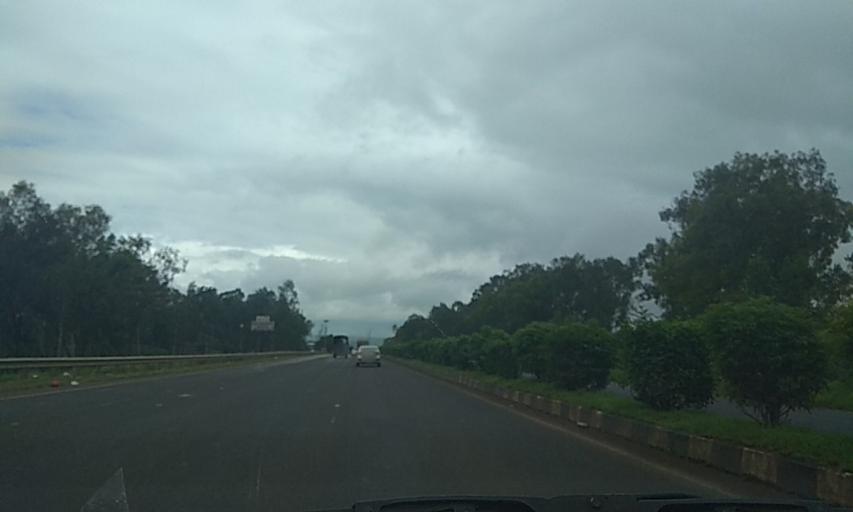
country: IN
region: Karnataka
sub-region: Belgaum
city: Belgaum
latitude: 15.8902
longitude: 74.5241
